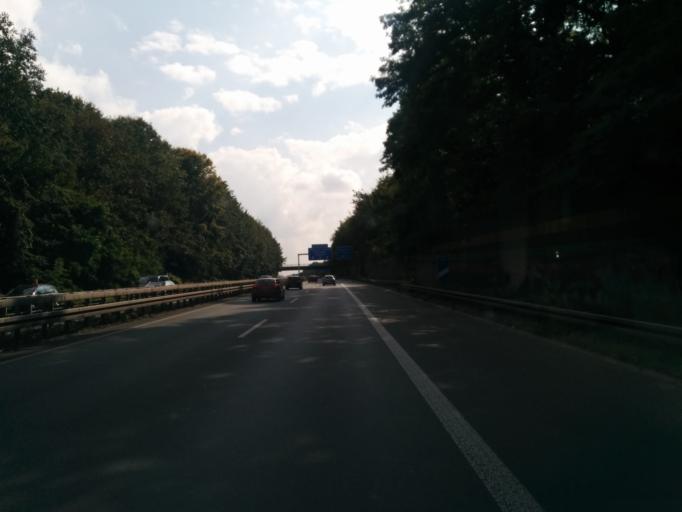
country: DE
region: North Rhine-Westphalia
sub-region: Regierungsbezirk Munster
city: Recklinghausen
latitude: 51.5913
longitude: 7.1871
